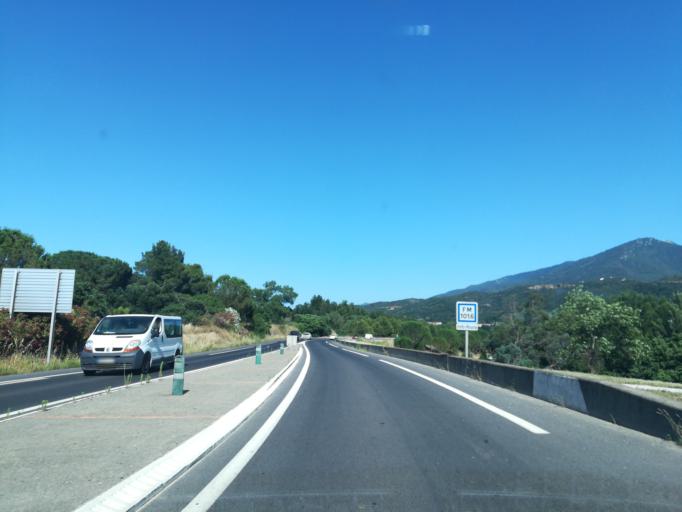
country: FR
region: Languedoc-Roussillon
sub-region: Departement des Pyrenees-Orientales
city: el Volo
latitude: 42.5200
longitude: 2.8238
